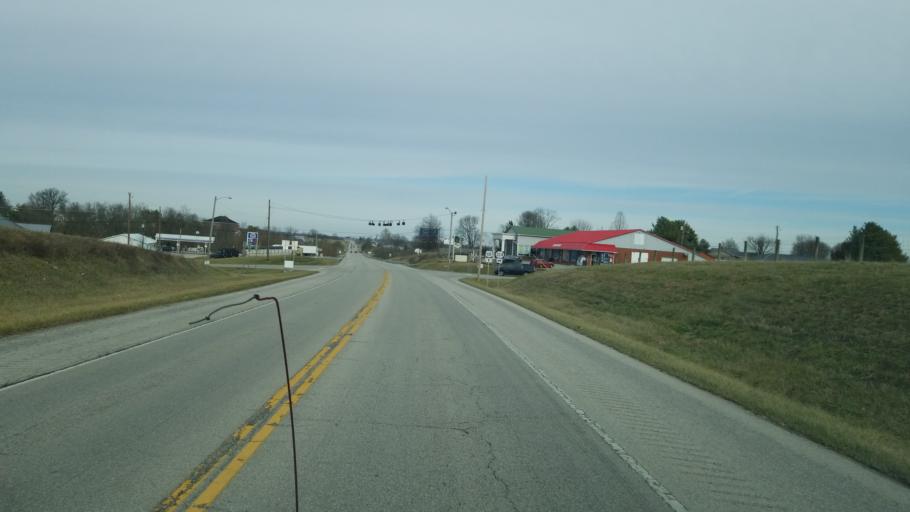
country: US
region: Kentucky
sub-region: Fleming County
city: Flemingsburg
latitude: 38.5167
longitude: -83.8384
